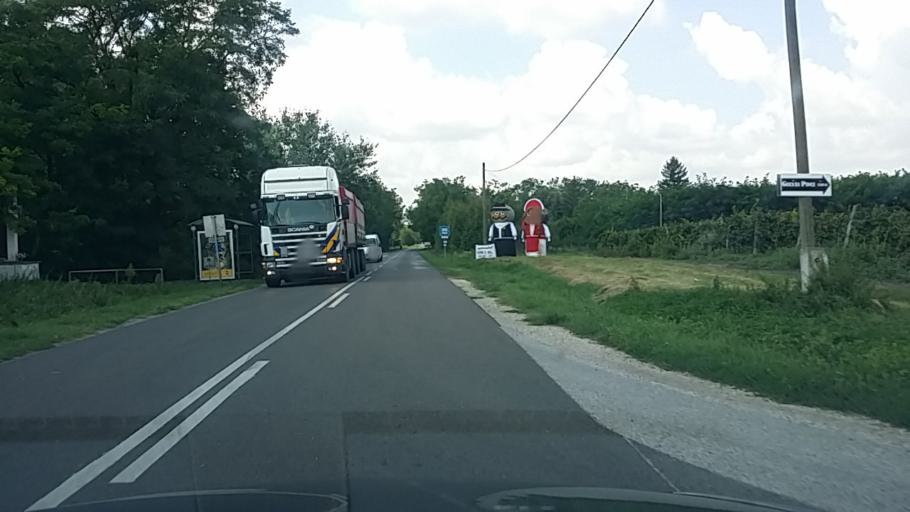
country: HU
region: Bacs-Kiskun
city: Tiszaalpar
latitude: 46.7457
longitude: 20.0462
